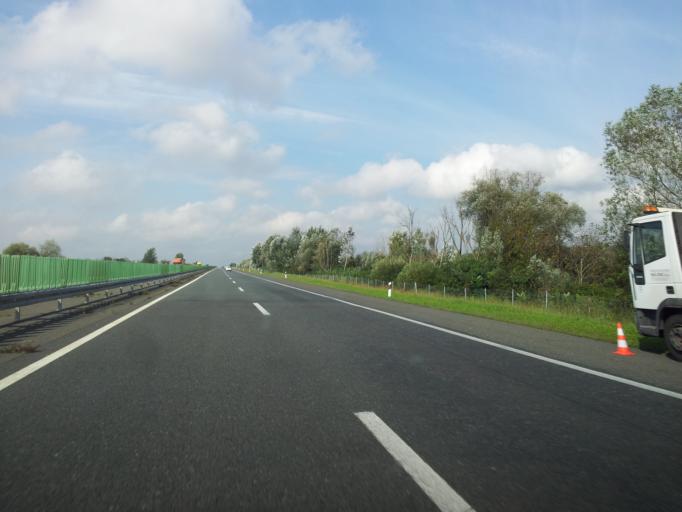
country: HR
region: Brodsko-Posavska
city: Garcin
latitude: 45.1725
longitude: 18.1495
